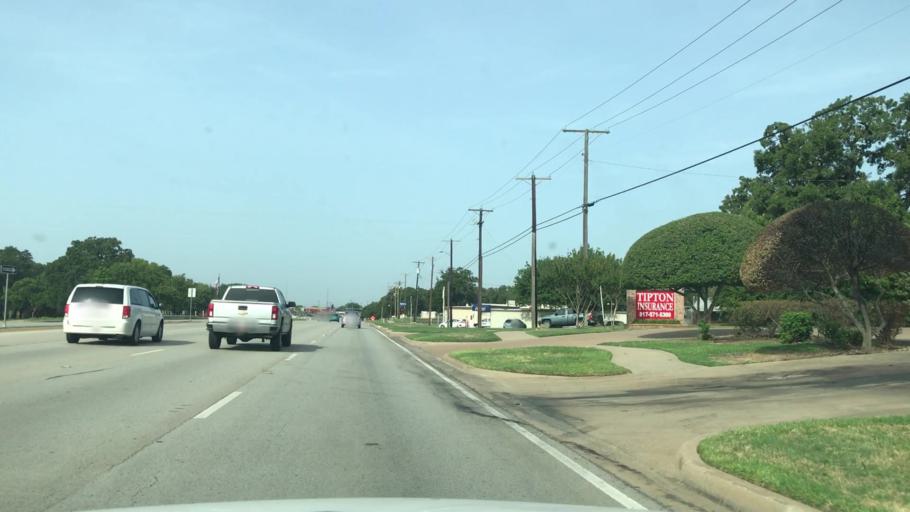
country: US
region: Texas
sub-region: Tarrant County
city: Euless
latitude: 32.8328
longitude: -97.0926
